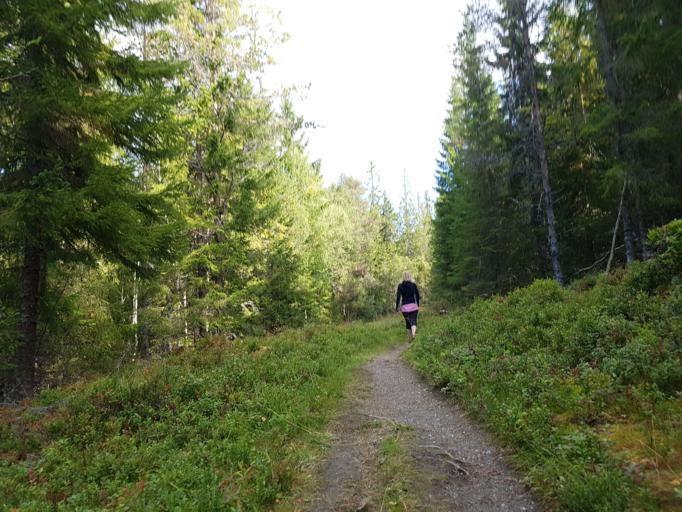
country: NO
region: Sor-Trondelag
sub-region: Trondheim
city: Trondheim
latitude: 63.4355
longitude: 10.2861
